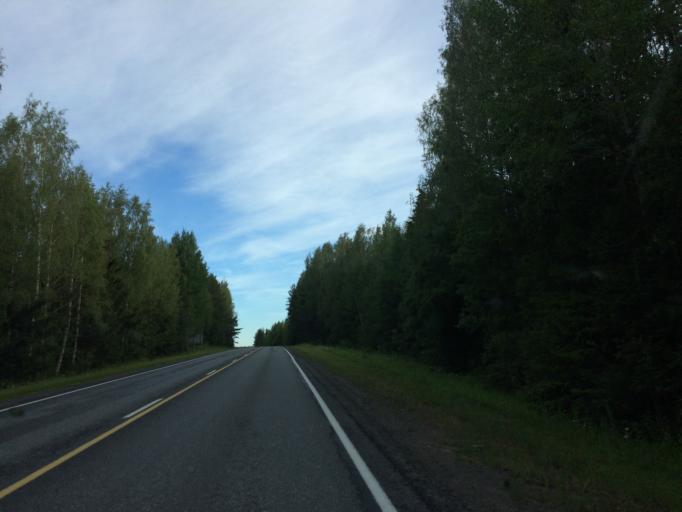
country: FI
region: Haeme
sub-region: Haemeenlinna
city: Janakkala
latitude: 60.8841
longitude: 24.5714
